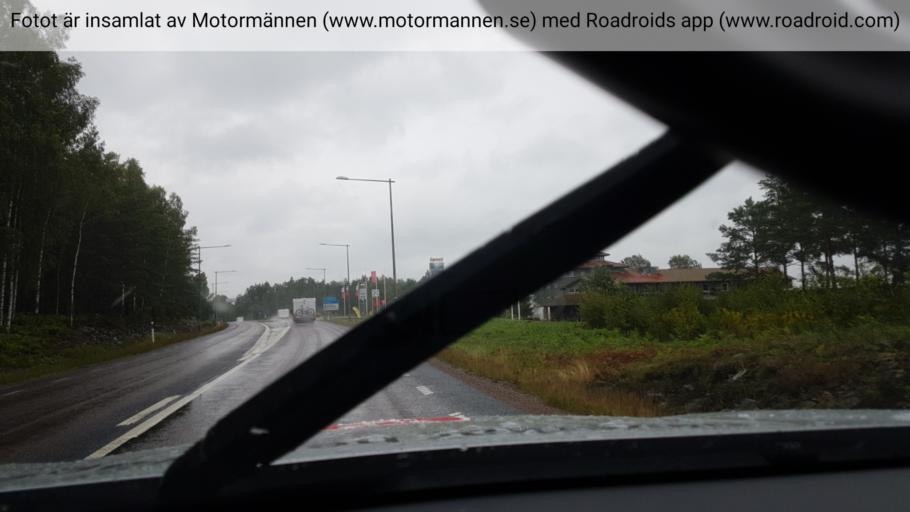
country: SE
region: Vaestra Goetaland
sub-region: Amals Kommun
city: Amal
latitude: 59.0445
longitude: 12.6779
